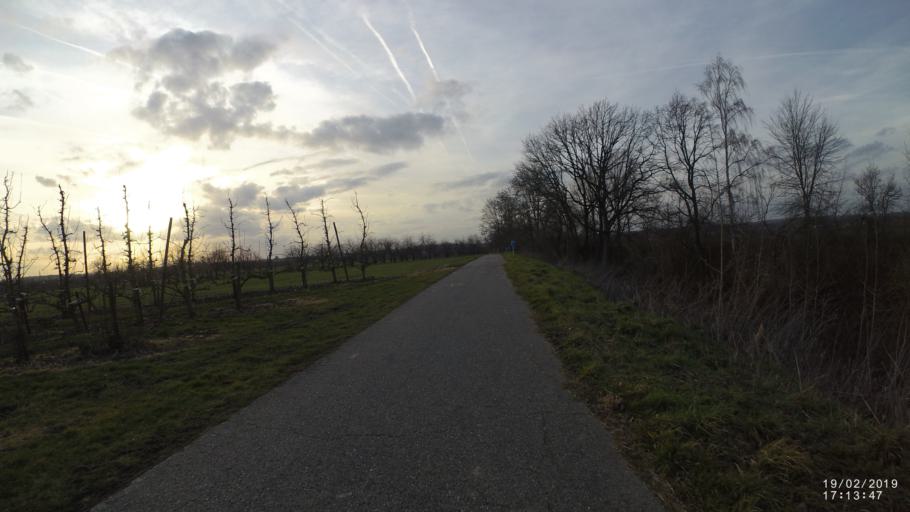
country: BE
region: Flanders
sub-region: Provincie Limburg
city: Sint-Truiden
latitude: 50.8138
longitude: 5.2569
